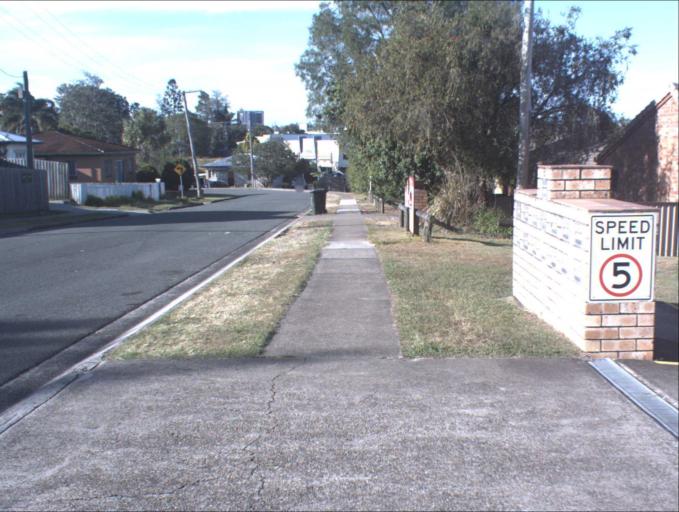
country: AU
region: Queensland
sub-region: Logan
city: Beenleigh
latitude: -27.7221
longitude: 153.2021
